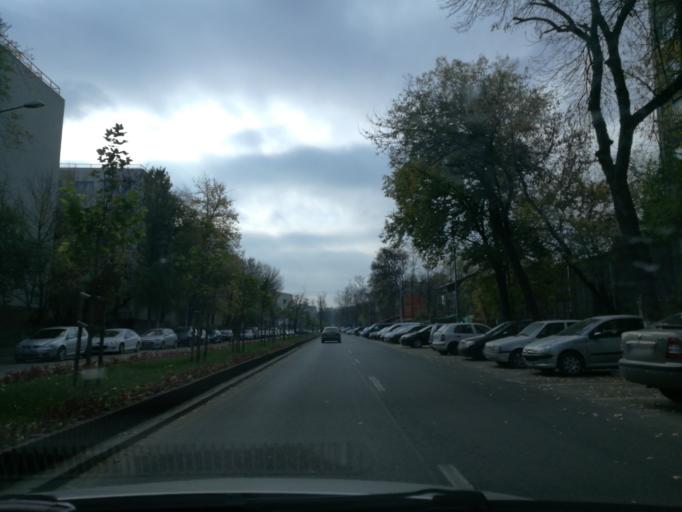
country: RO
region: Ilfov
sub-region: Comuna Chiajna
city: Rosu
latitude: 44.4404
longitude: 26.0167
